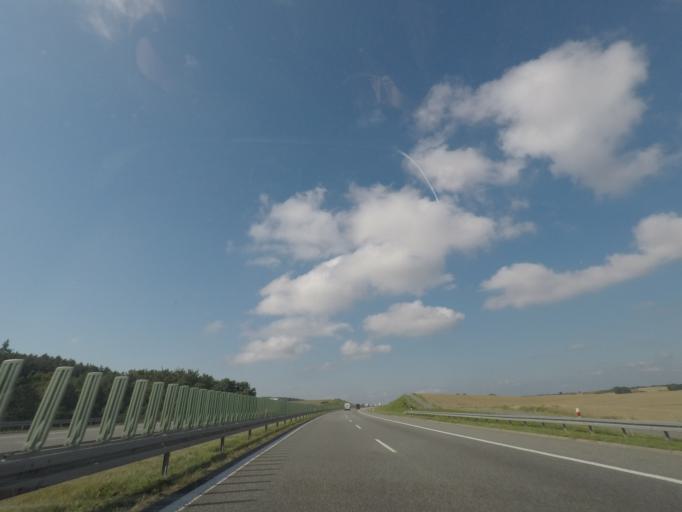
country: PL
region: Pomeranian Voivodeship
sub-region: Powiat tczewski
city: Tczew
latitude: 54.0765
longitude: 18.6867
